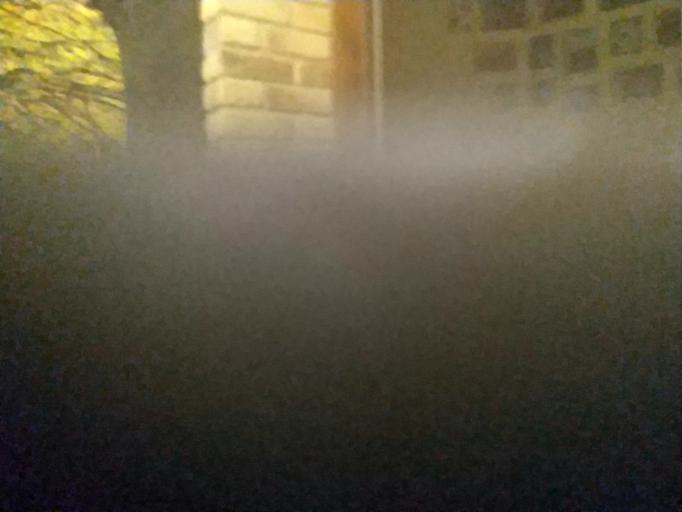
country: RU
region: Moskovskaya
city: Vysokovsk
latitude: 56.2553
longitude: 36.4996
